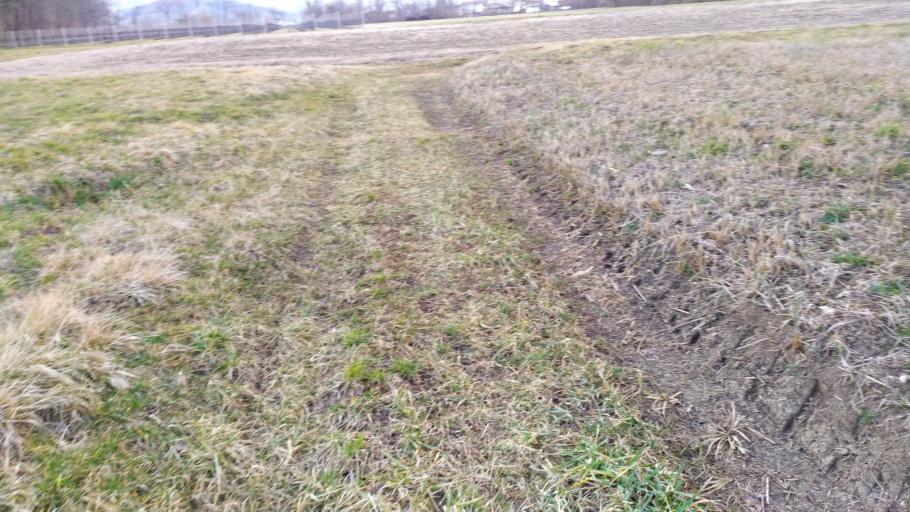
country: IT
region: Veneto
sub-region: Provincia di Treviso
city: Covolo-Levada
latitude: 45.8433
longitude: 12.0022
